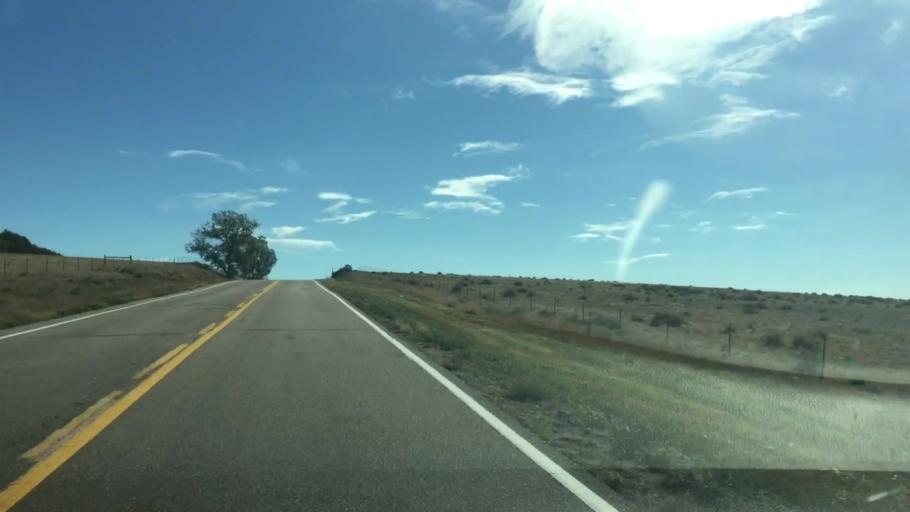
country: US
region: Colorado
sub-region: Elbert County
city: Kiowa
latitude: 39.2736
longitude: -104.2120
